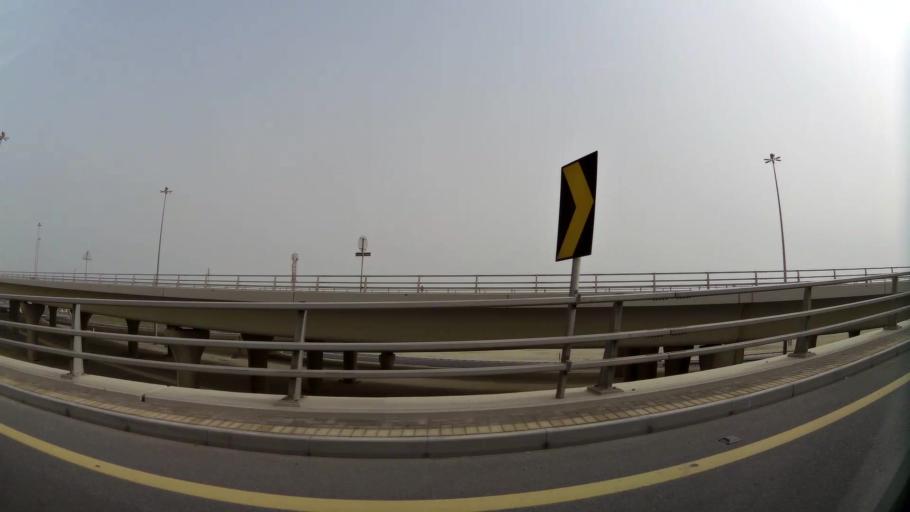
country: BH
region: Muharraq
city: Al Muharraq
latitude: 26.2448
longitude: 50.5912
